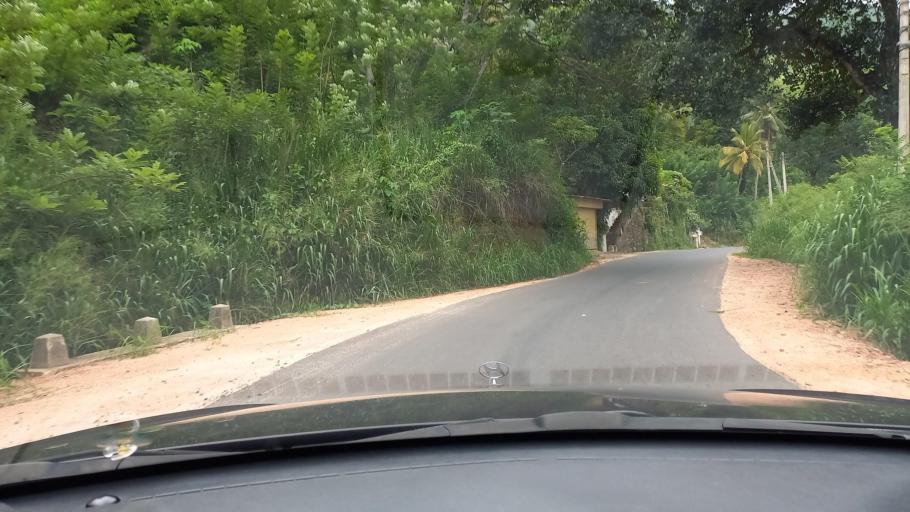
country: LK
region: Central
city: Gampola
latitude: 7.2048
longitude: 80.6273
